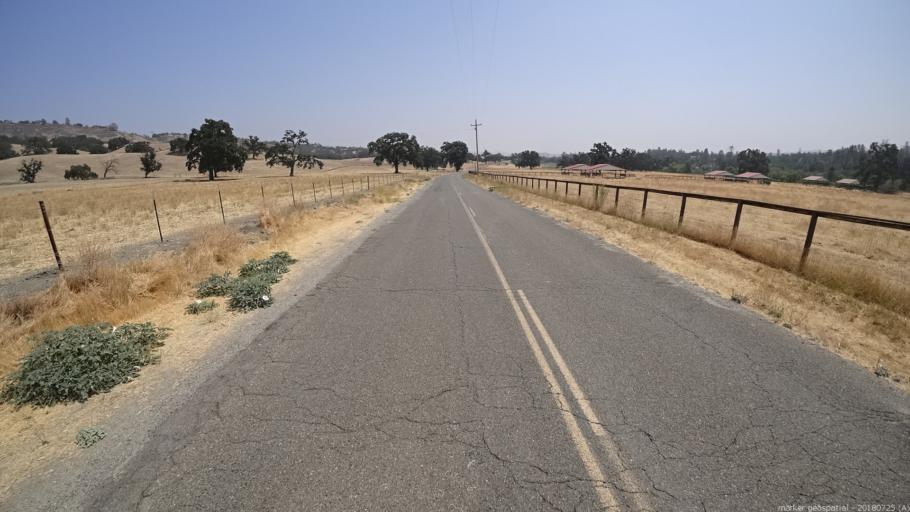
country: US
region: California
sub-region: Fresno County
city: Coalinga
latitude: 35.9109
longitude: -120.4704
